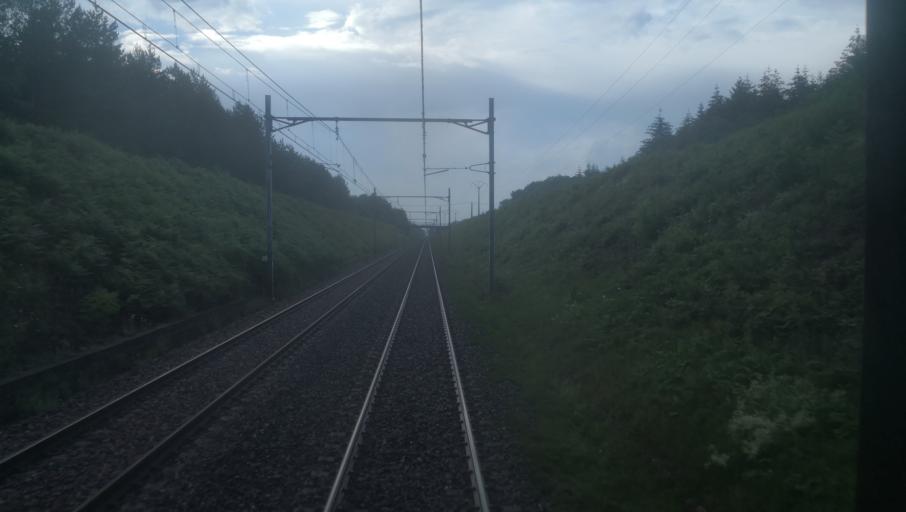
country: FR
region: Centre
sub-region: Departement du Loir-et-Cher
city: Lamotte-Beuvron
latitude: 47.6427
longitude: 1.9891
